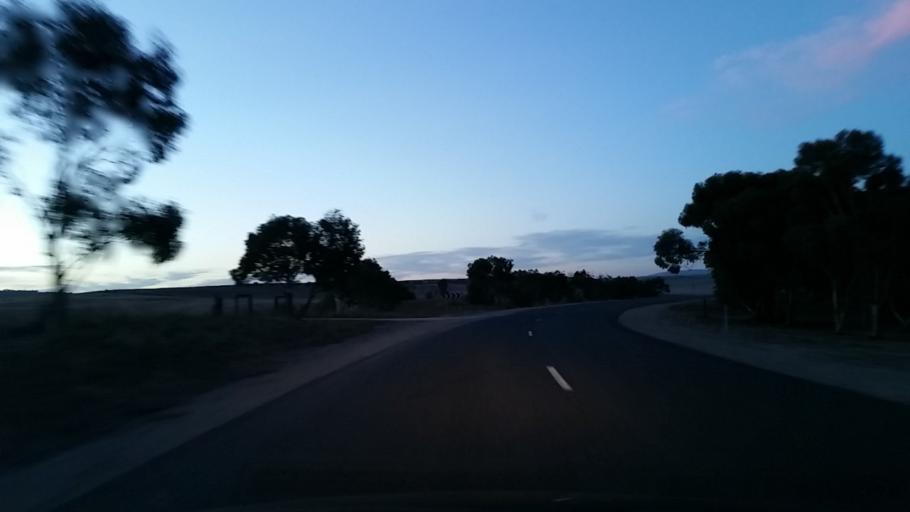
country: AU
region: South Australia
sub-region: Mount Barker
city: Callington
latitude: -35.1091
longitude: 139.0375
